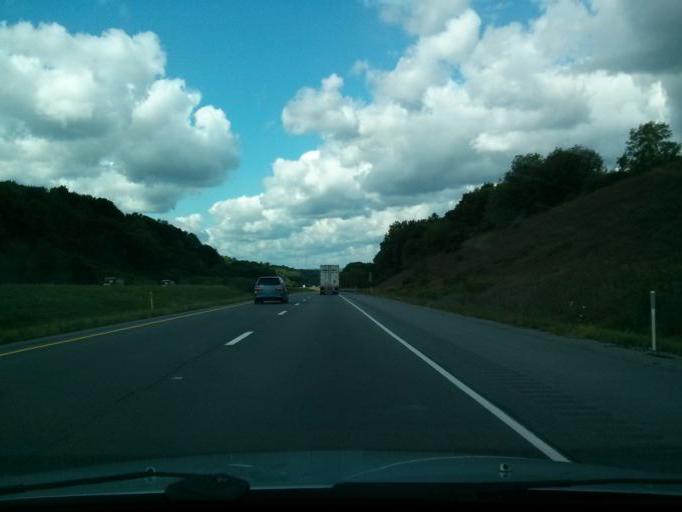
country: US
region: Pennsylvania
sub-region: Clearfield County
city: Treasure Lake
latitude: 41.1218
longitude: -78.6569
